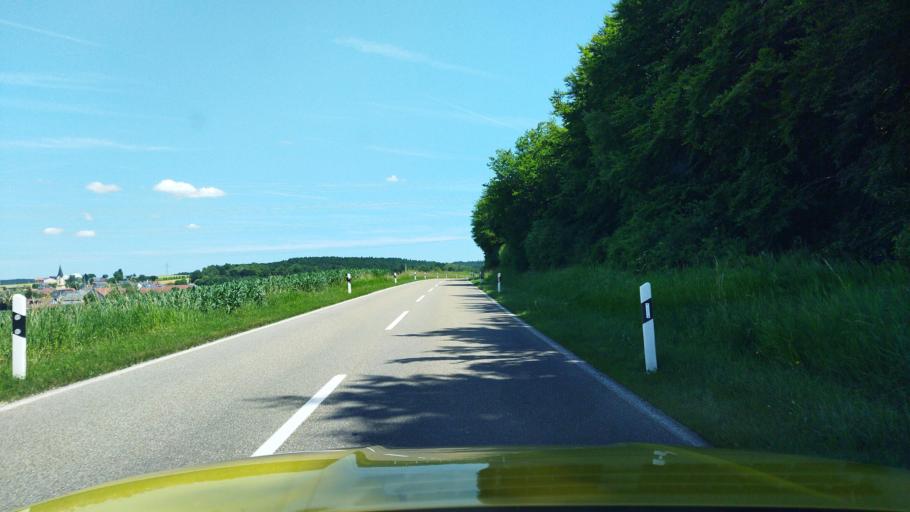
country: DE
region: Bavaria
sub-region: Lower Bavaria
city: Riedenburg
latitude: 48.9527
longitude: 11.6168
